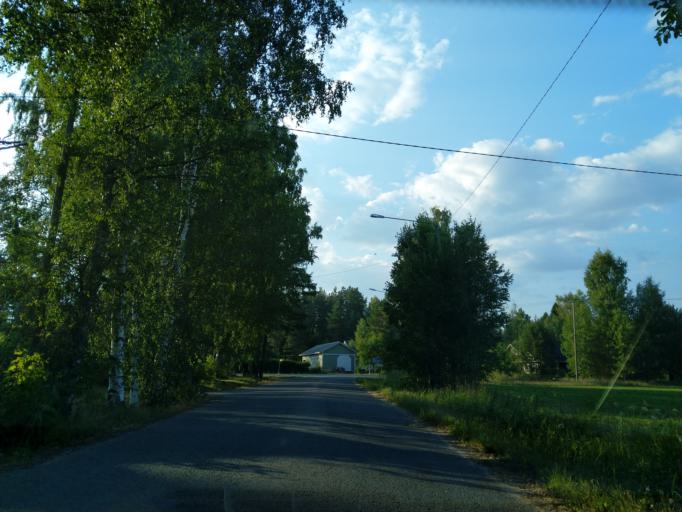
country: FI
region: Satakunta
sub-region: Pohjois-Satakunta
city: Honkajoki
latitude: 61.8201
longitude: 22.1993
